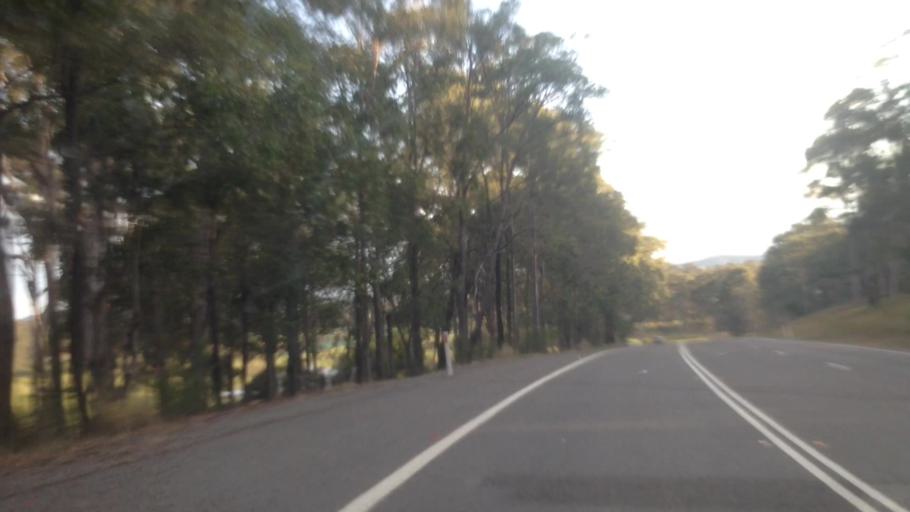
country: AU
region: New South Wales
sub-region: Cessnock
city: Kurri Kurri
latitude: -32.8610
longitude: 151.4833
